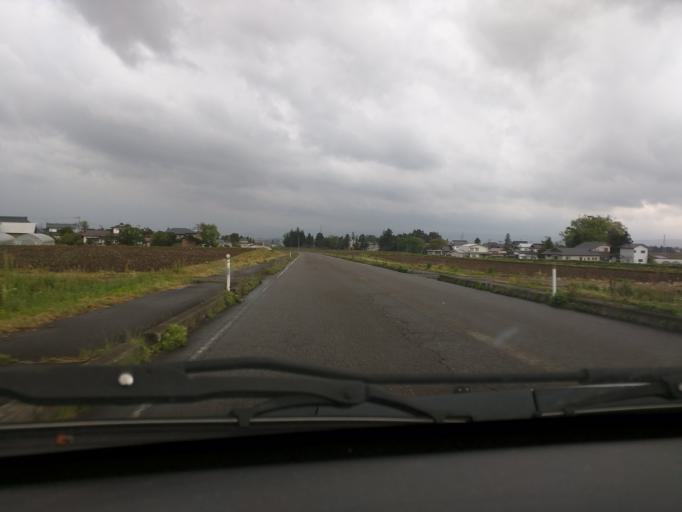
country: JP
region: Fukushima
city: Kitakata
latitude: 37.6167
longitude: 139.9140
